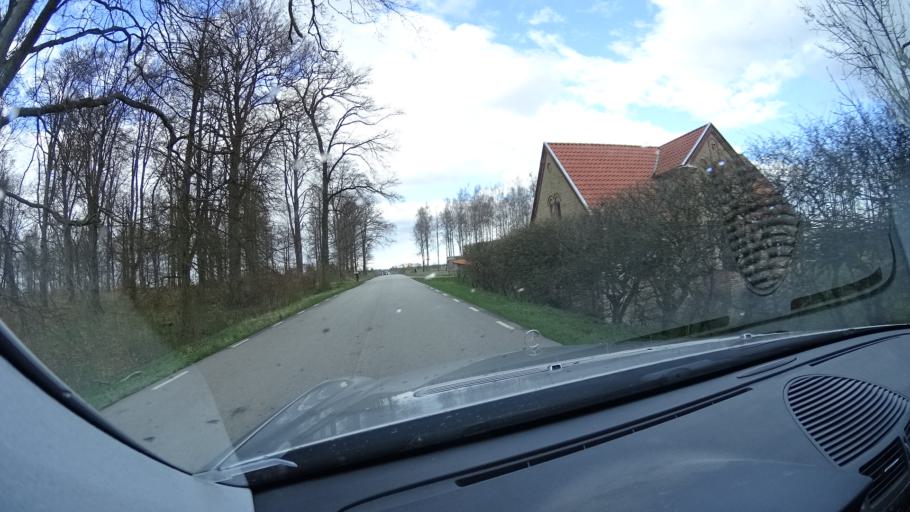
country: SE
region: Skane
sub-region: Eslovs Kommun
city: Eslov
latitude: 55.8067
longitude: 13.3741
